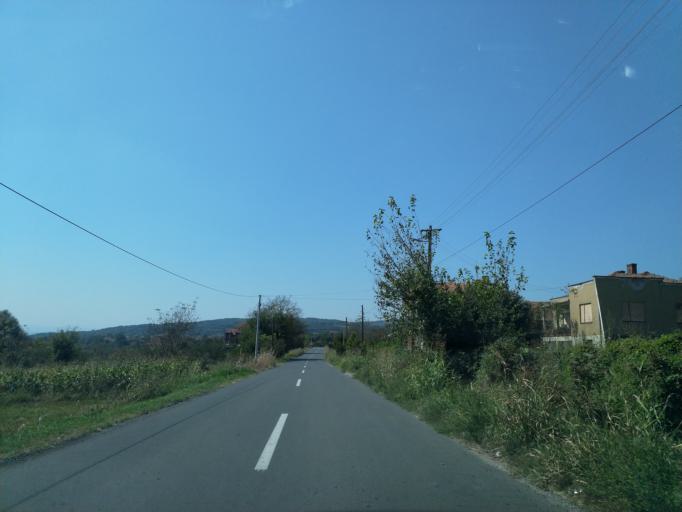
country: RS
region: Central Serbia
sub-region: Rasinski Okrug
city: Krusevac
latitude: 43.6214
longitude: 21.3150
